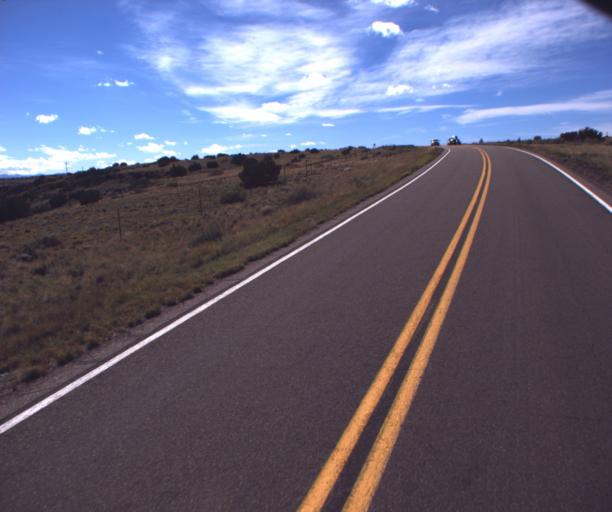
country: US
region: Arizona
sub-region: Apache County
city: Saint Johns
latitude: 34.4996
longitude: -109.5005
